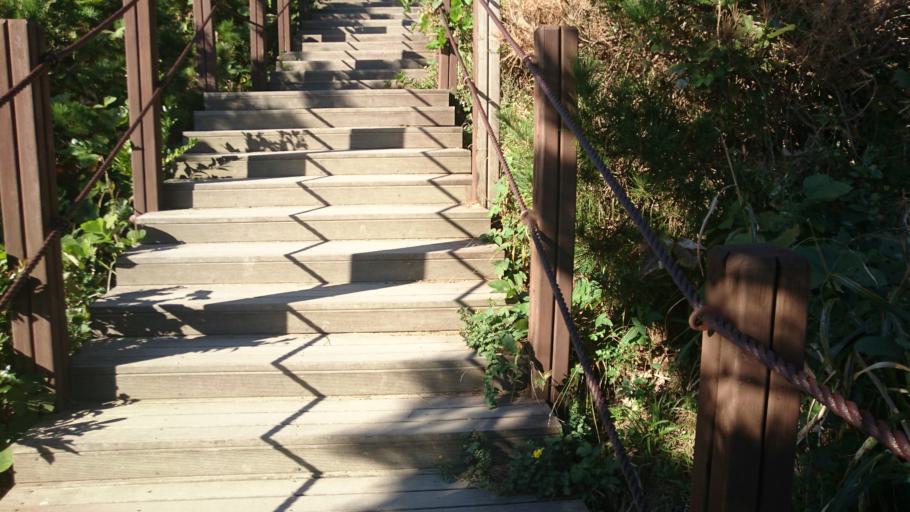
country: KR
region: Gyeongsangnam-do
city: Kyosai
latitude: 34.6261
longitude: 128.5508
